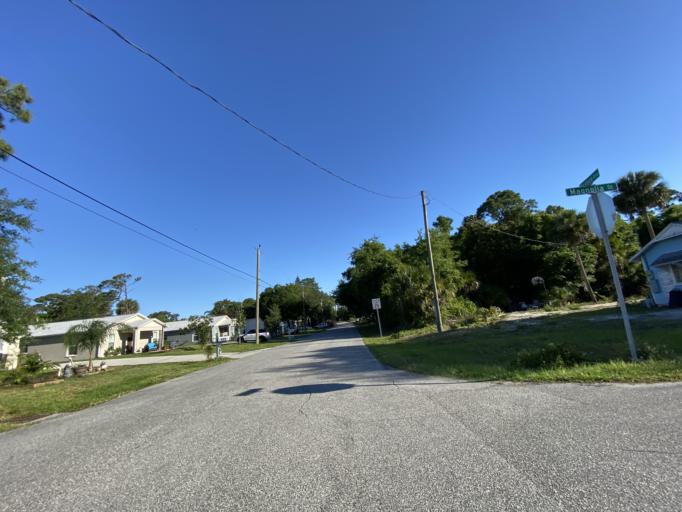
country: US
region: Florida
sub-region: Volusia County
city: Port Orange
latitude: 29.1478
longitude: -80.9936
